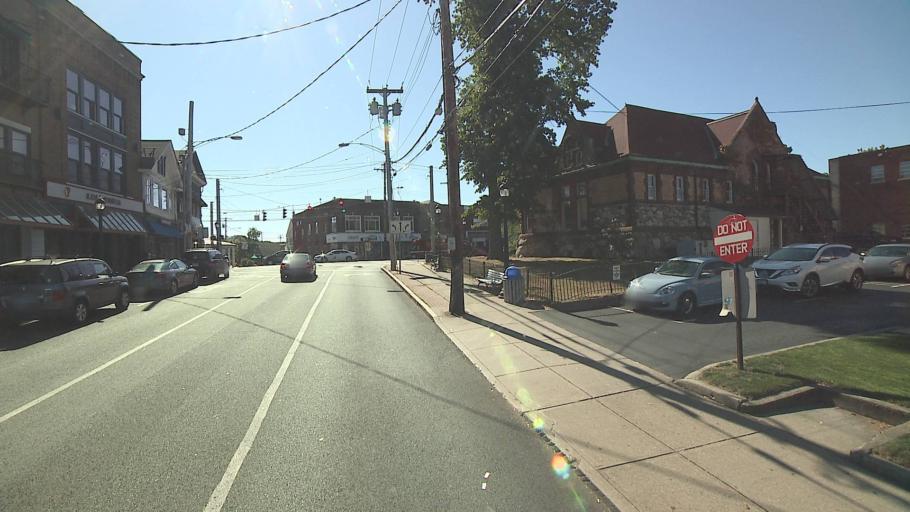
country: US
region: Connecticut
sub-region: New Haven County
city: Milford
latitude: 41.2228
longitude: -73.0570
